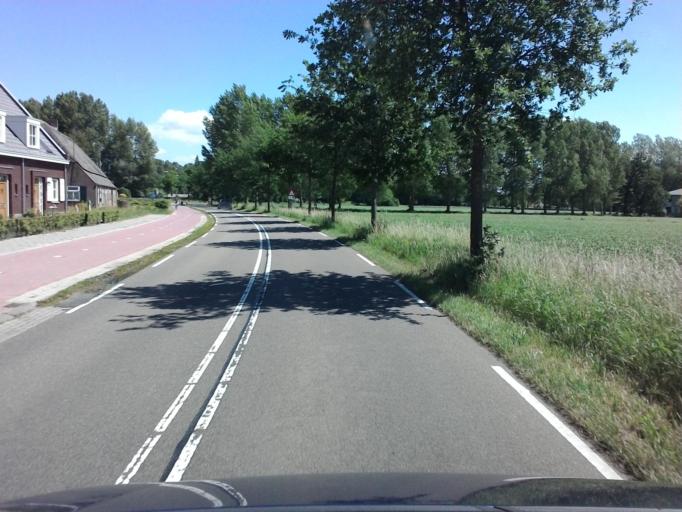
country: NL
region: North Brabant
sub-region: Gemeente Sint-Michielsgestel
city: Sint-Michielsgestel
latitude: 51.6382
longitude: 5.3654
